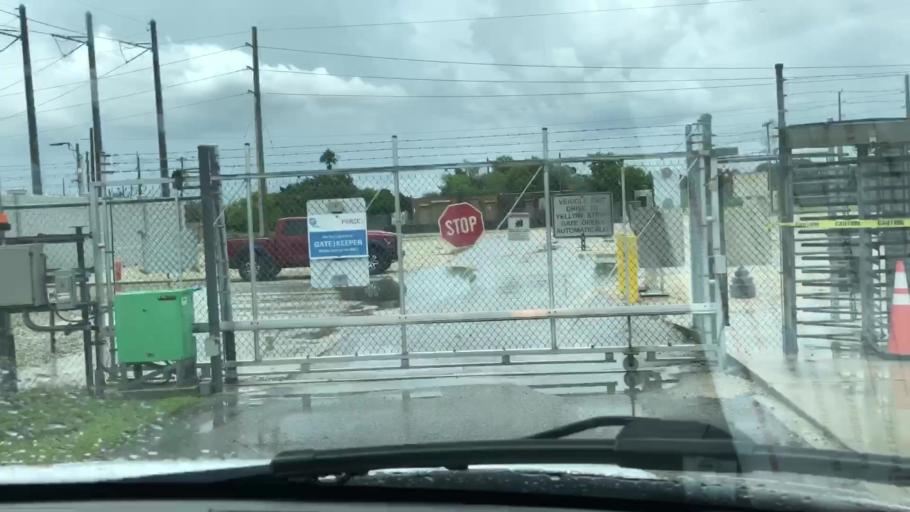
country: US
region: Florida
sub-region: Lee County
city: Fort Myers Shores
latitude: 26.6982
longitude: -81.7812
